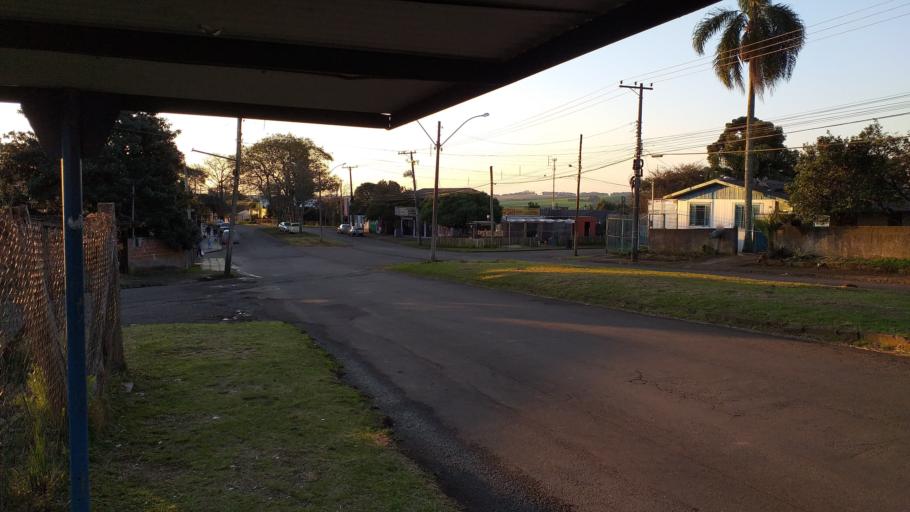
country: BR
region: Rio Grande do Sul
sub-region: Passo Fundo
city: Passo Fundo
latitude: -28.2335
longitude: -52.3700
